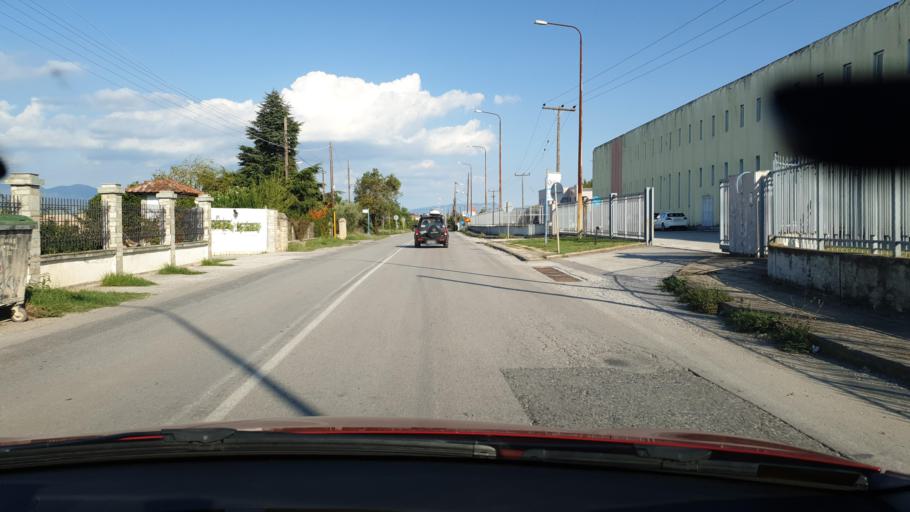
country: GR
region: Central Macedonia
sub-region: Nomos Thessalonikis
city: Neo Rysi
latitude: 40.4946
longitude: 23.0111
